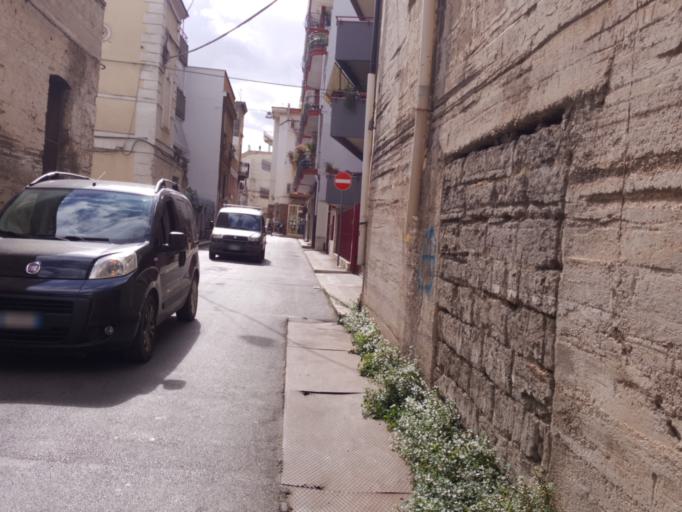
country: IT
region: Apulia
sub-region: Provincia di Bari
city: Triggiano
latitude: 41.0659
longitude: 16.9211
